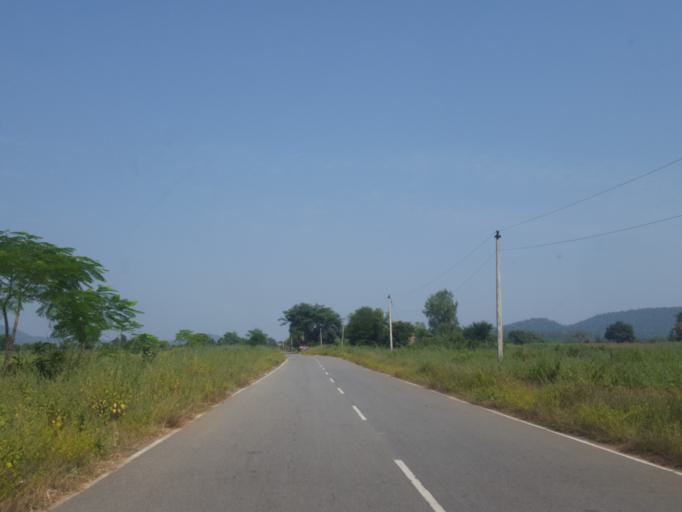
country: IN
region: Telangana
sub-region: Khammam
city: Yellandu
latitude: 17.6589
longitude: 80.2771
